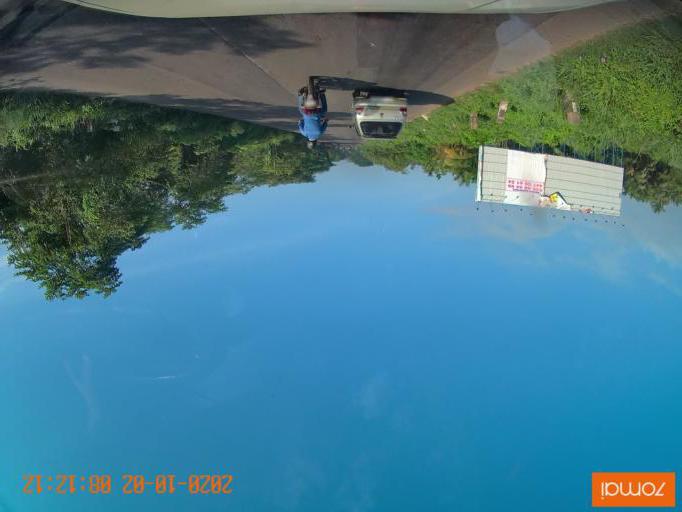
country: IN
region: Kerala
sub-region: Kozhikode
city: Kozhikode
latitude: 11.2795
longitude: 75.8047
